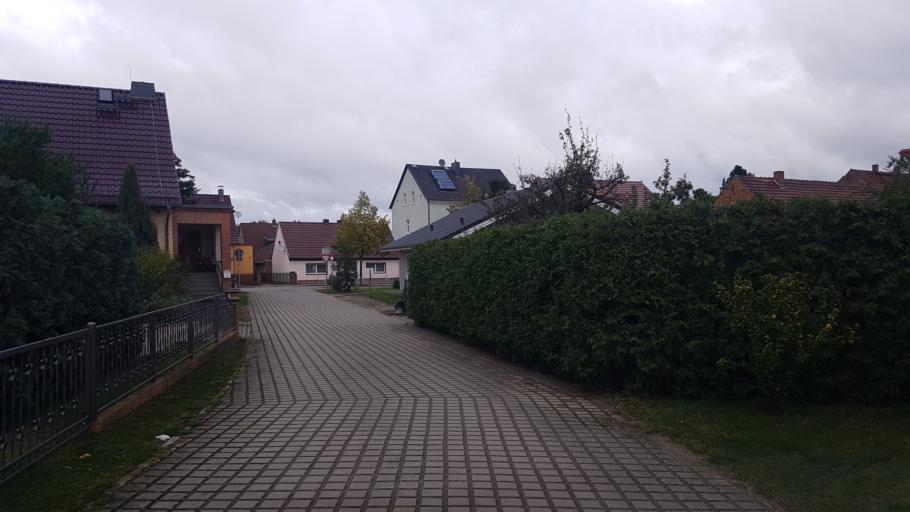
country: DE
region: Brandenburg
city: Altdobern
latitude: 51.6477
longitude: 14.0275
